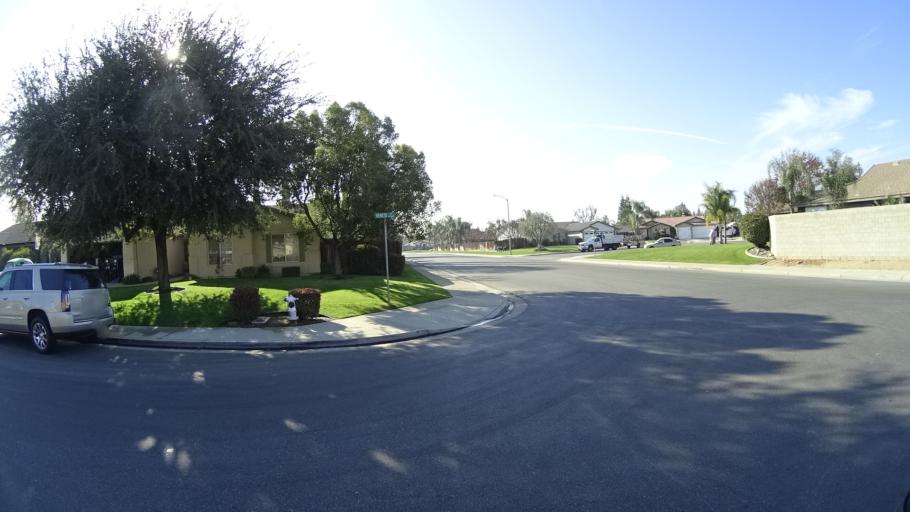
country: US
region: California
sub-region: Kern County
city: Oildale
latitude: 35.4053
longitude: -119.0654
